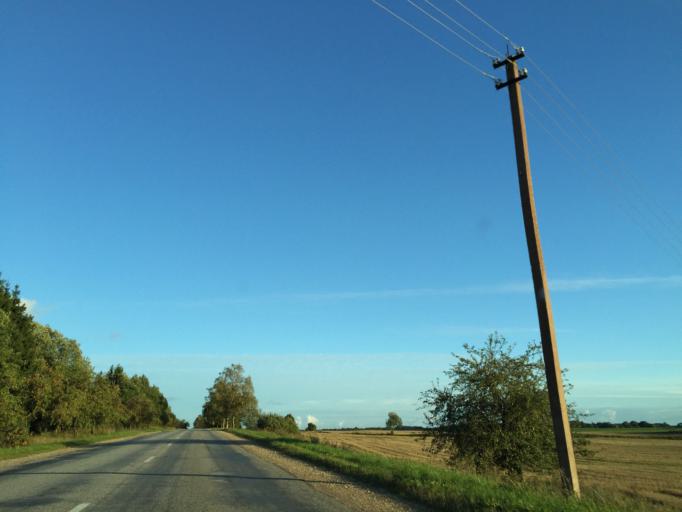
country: LV
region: Saldus Rajons
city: Saldus
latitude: 56.7223
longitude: 22.3851
